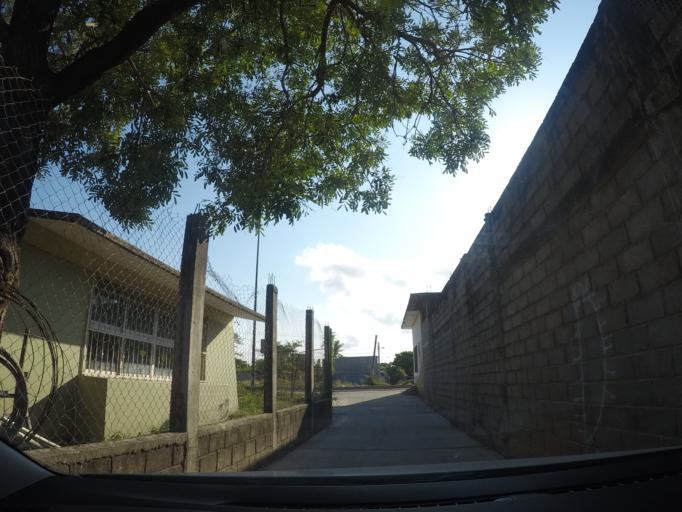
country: MX
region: Oaxaca
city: Juchitan de Zaragoza
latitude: 16.4212
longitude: -95.0276
